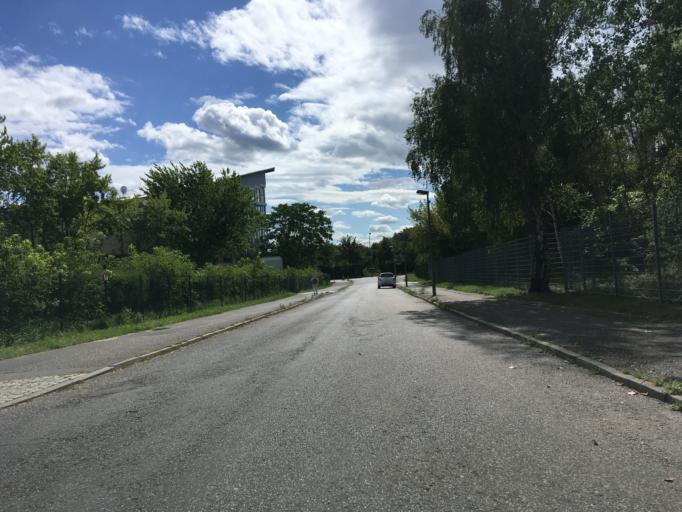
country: DE
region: Berlin
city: Staaken
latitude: 52.5374
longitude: 13.1301
